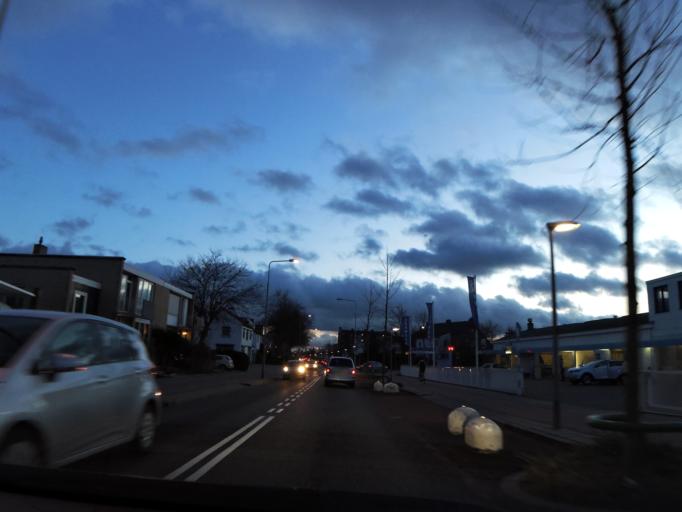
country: NL
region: Limburg
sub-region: Gemeente Roermond
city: Leeuwen
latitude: 51.1962
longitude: 6.0038
